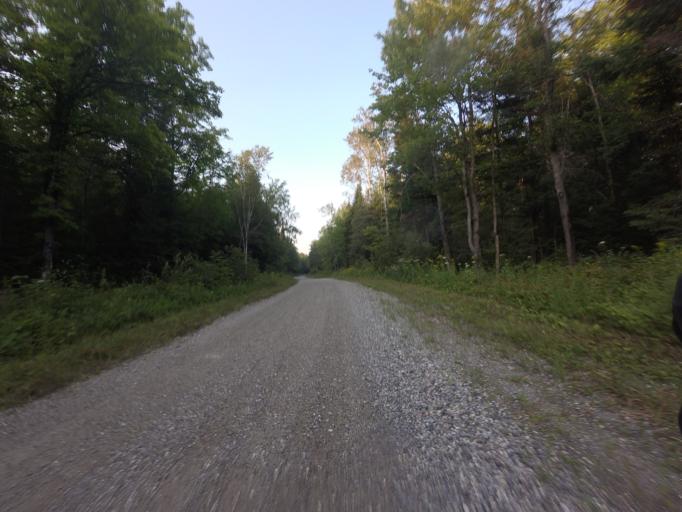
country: CA
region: Ontario
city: Renfrew
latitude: 45.0756
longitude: -76.7368
